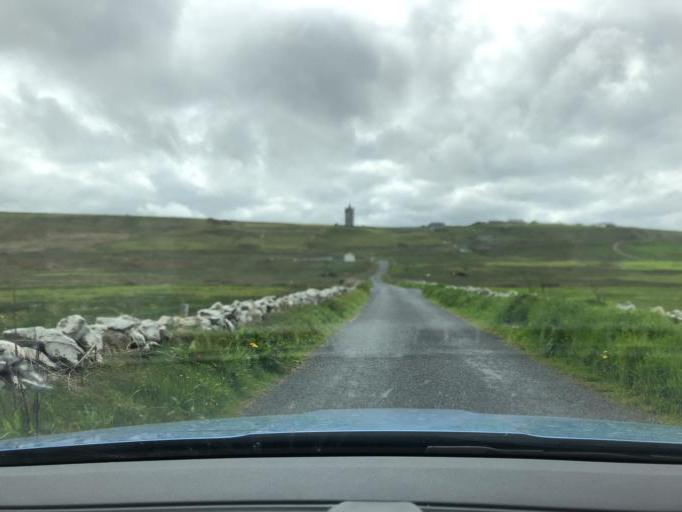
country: IE
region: Connaught
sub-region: County Galway
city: Bearna
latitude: 53.0084
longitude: -9.3886
